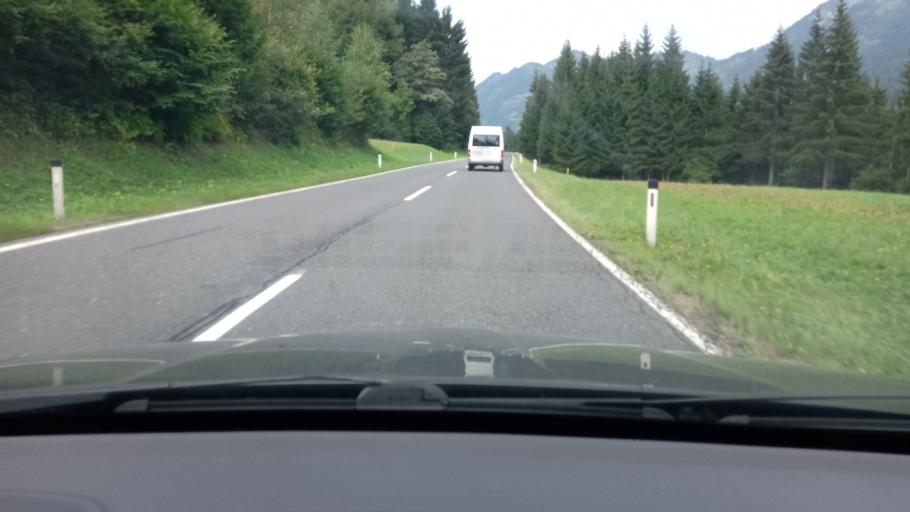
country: AT
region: Carinthia
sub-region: Politischer Bezirk Hermagor
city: Hermagor
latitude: 46.6495
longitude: 13.3296
